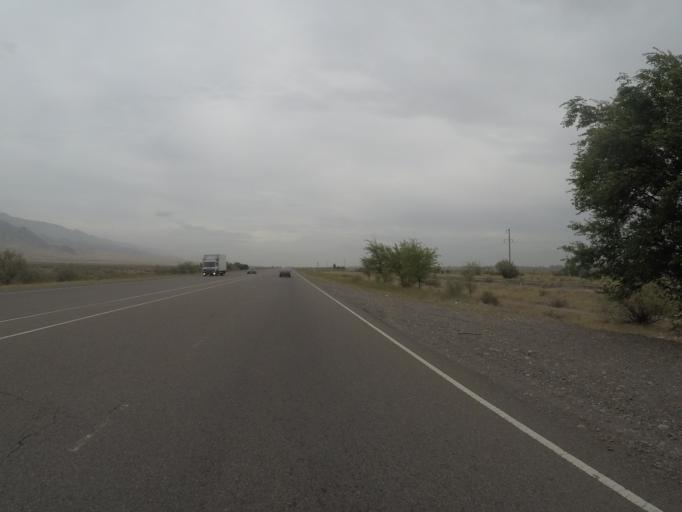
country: KG
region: Chuy
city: Tokmok
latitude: 42.8295
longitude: 75.4811
